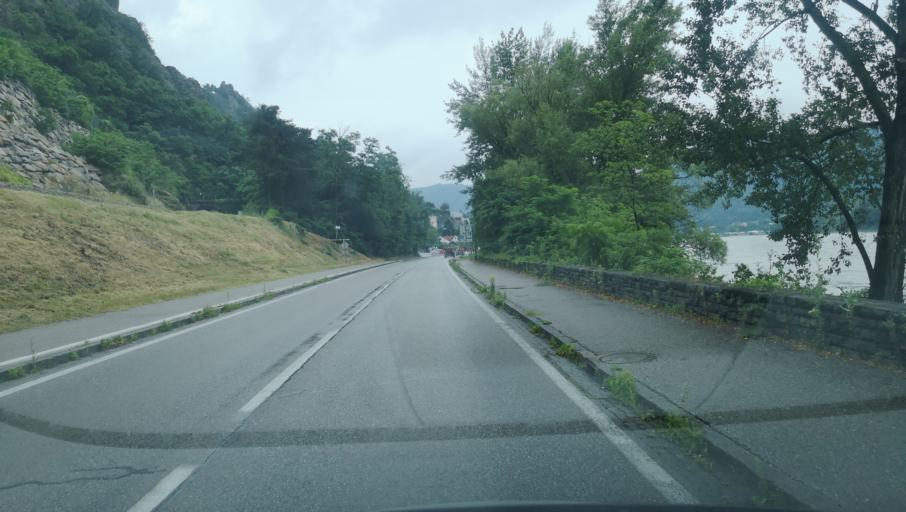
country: AT
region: Lower Austria
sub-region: Politischer Bezirk Krems
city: Durnstein
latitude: 48.4012
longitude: 15.5171
